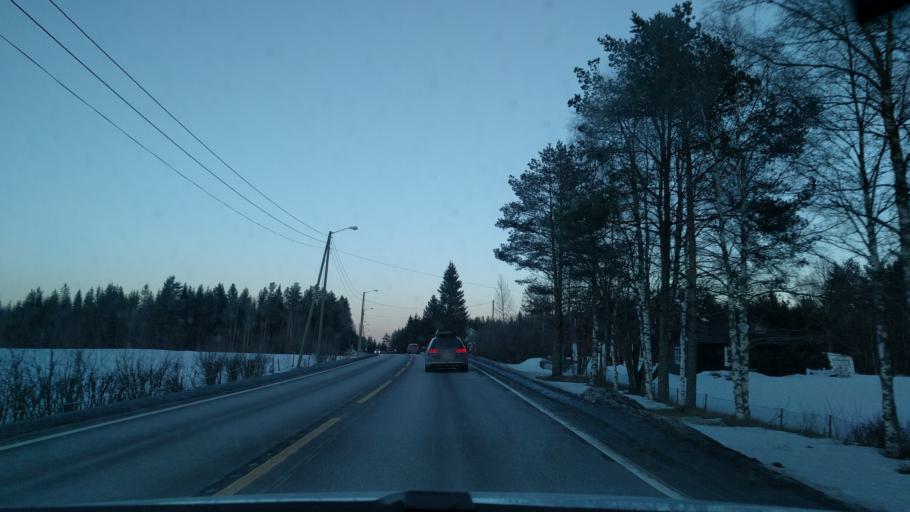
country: NO
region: Hedmark
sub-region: Elverum
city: Elverum
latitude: 60.8770
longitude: 11.4713
